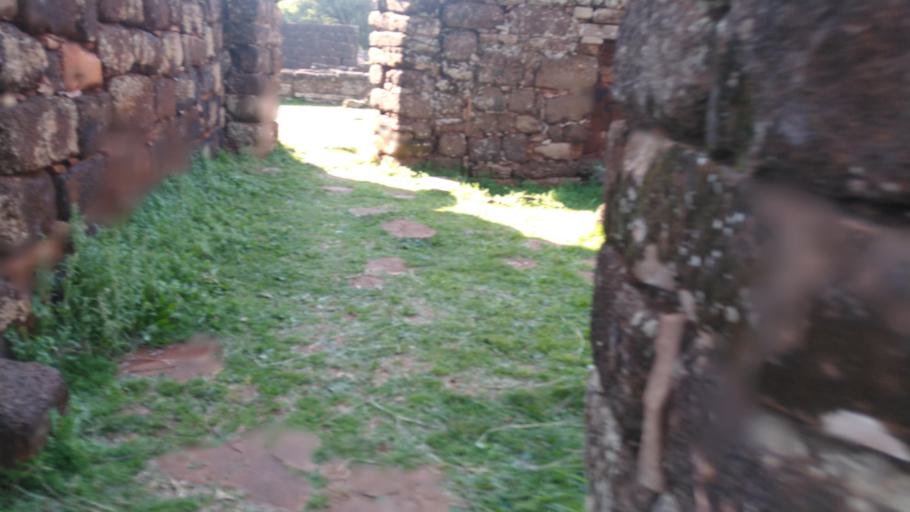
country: AR
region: Misiones
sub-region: Departamento de San Ignacio
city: San Ignacio
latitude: -27.2557
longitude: -55.5310
